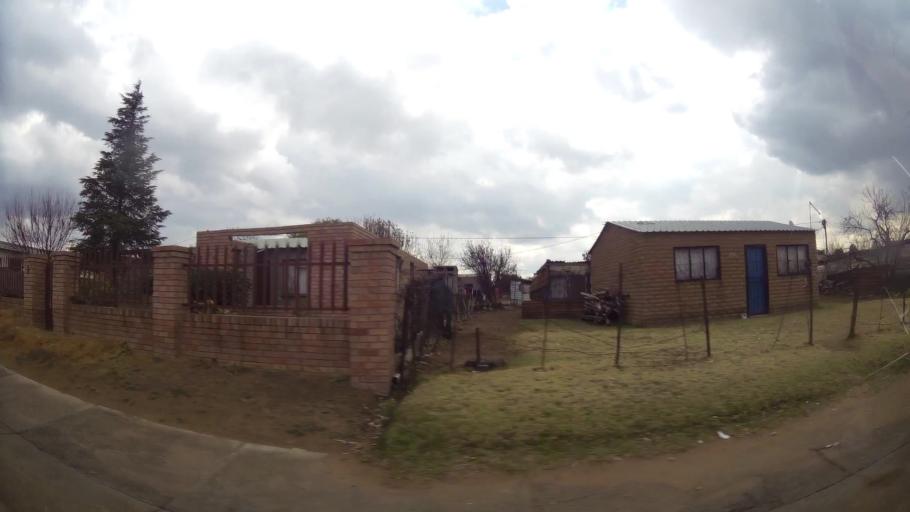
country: ZA
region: Orange Free State
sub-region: Fezile Dabi District Municipality
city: Sasolburg
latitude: -26.8488
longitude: 27.8781
